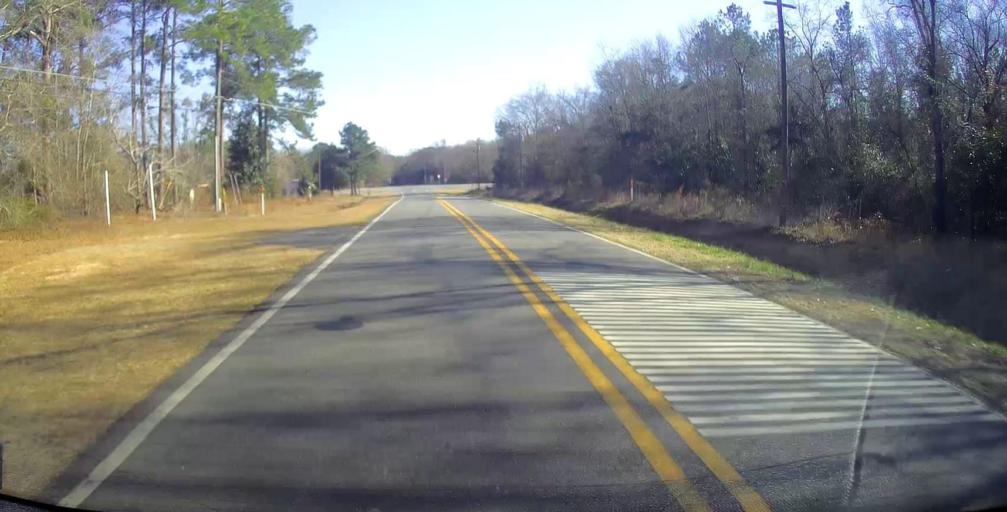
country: US
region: Georgia
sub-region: Taylor County
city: Butler
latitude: 32.5453
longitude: -84.2264
